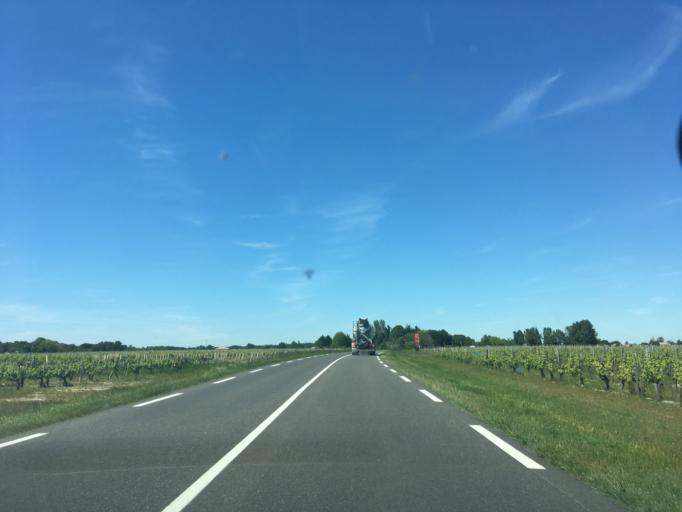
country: FR
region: Aquitaine
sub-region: Departement de la Gironde
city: Listrac-Medoc
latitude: 45.0632
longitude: -0.7950
